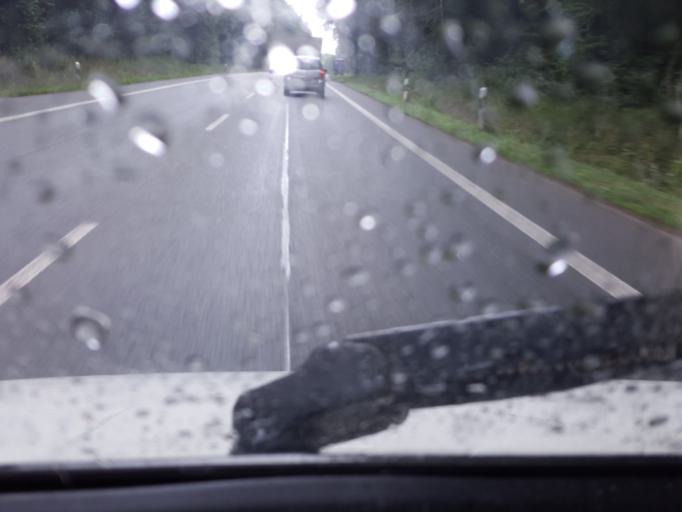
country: DE
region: North Rhine-Westphalia
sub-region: Regierungsbezirk Detmold
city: Petershagen
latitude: 52.3523
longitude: 8.9511
